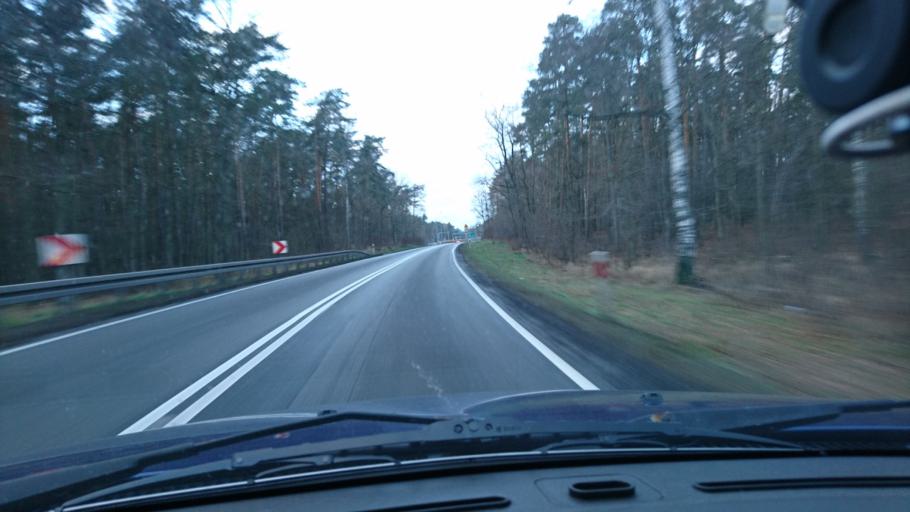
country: PL
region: Greater Poland Voivodeship
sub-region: Powiat kepinski
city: Kepno
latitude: 51.3282
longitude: 17.9612
